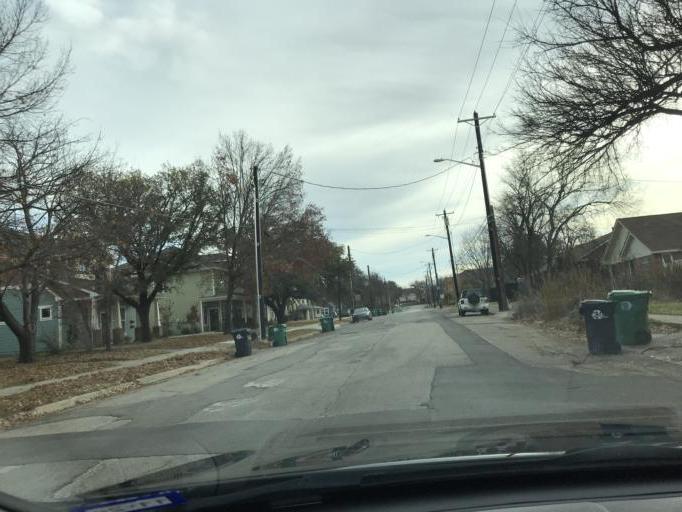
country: US
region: Texas
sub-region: Denton County
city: Denton
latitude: 33.2182
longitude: -97.1435
